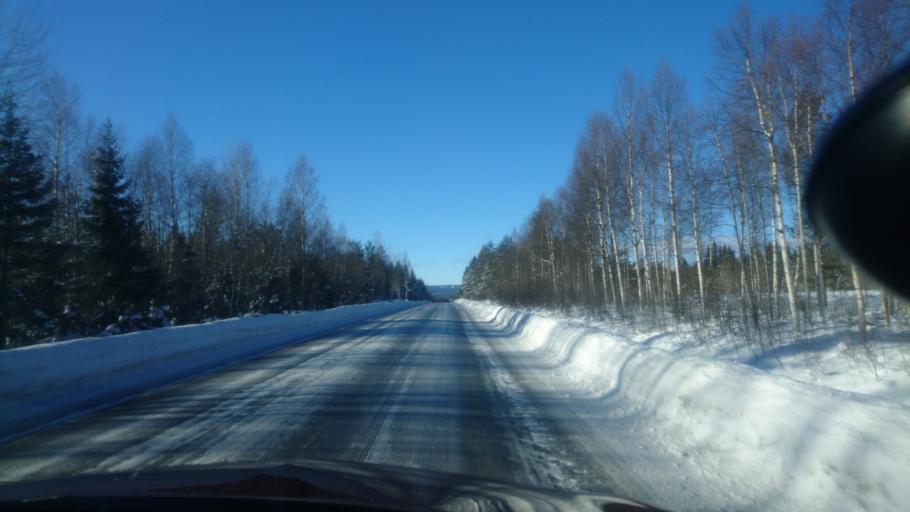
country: NO
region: Hedmark
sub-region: Trysil
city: Innbygda
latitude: 61.2650
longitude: 12.4292
